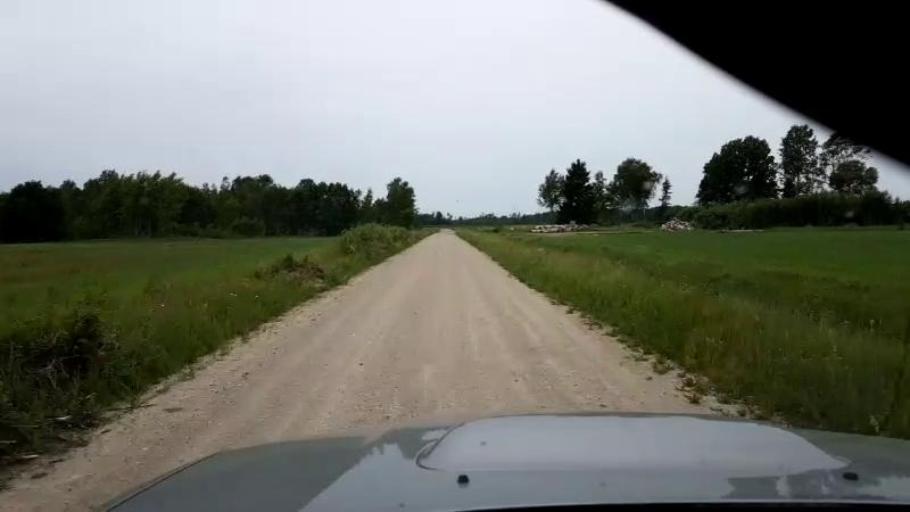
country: EE
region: Paernumaa
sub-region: Halinga vald
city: Parnu-Jaagupi
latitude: 58.5441
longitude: 24.6117
